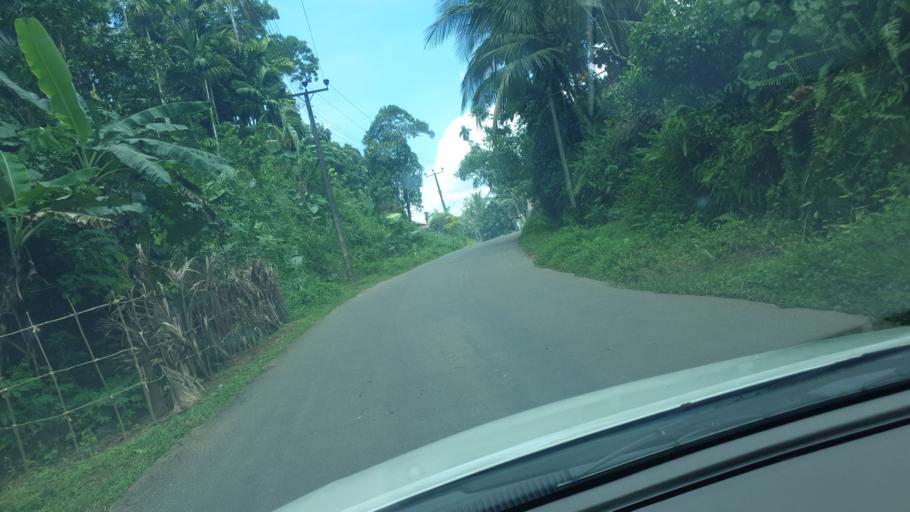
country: LK
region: Sabaragamuwa
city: Ratnapura
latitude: 6.4868
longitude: 80.4037
